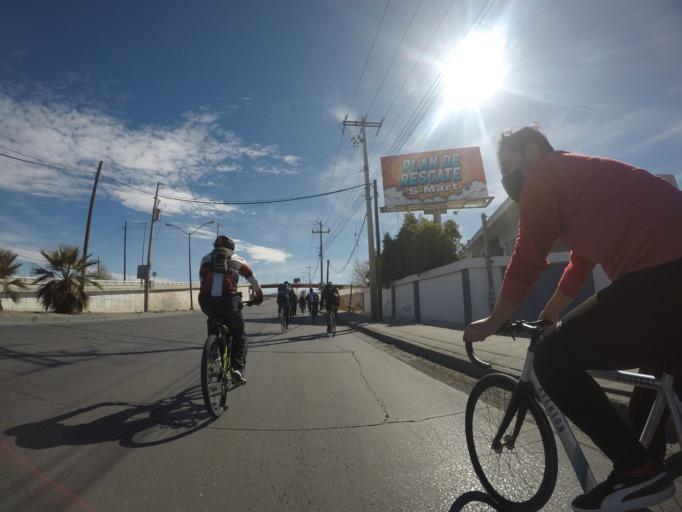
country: MX
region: Chihuahua
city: Ciudad Juarez
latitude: 31.6716
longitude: -106.4033
